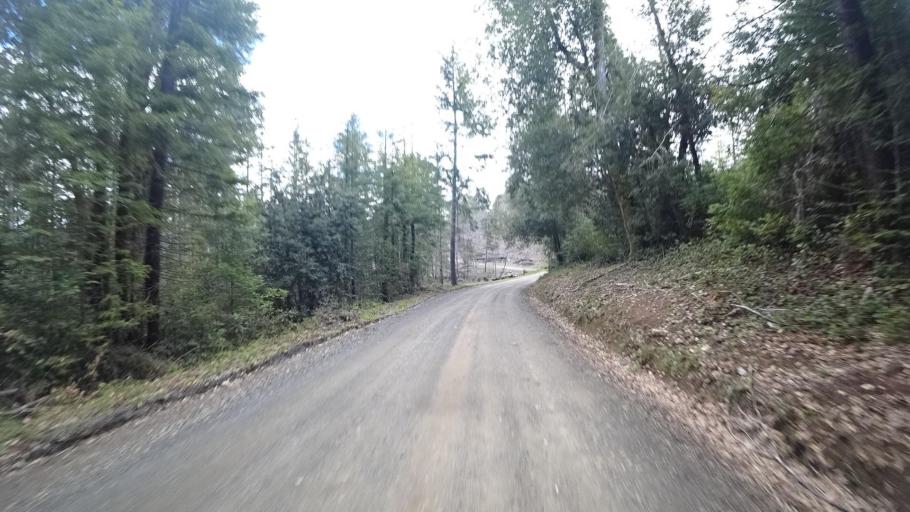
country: US
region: California
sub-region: Humboldt County
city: Blue Lake
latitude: 40.7701
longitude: -123.9556
